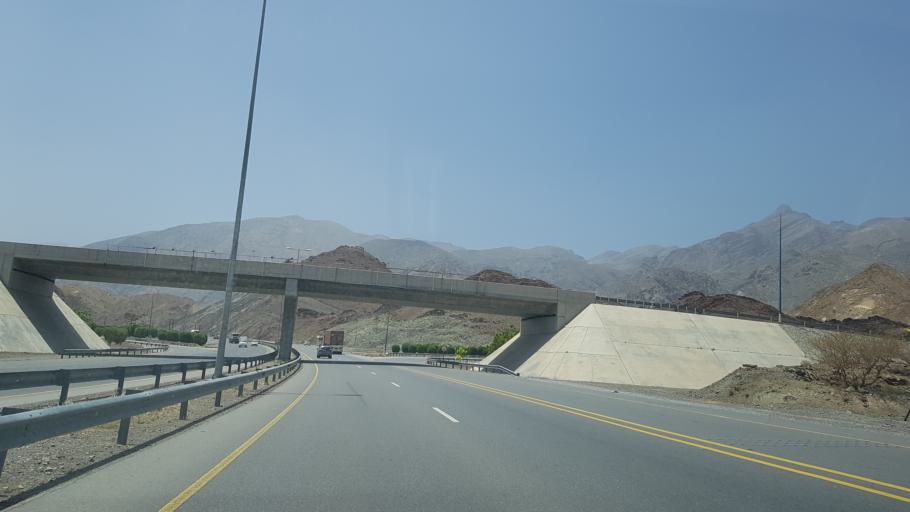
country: OM
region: Muhafazat ad Dakhiliyah
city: Sufalat Sama'il
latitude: 23.3160
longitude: 57.9502
